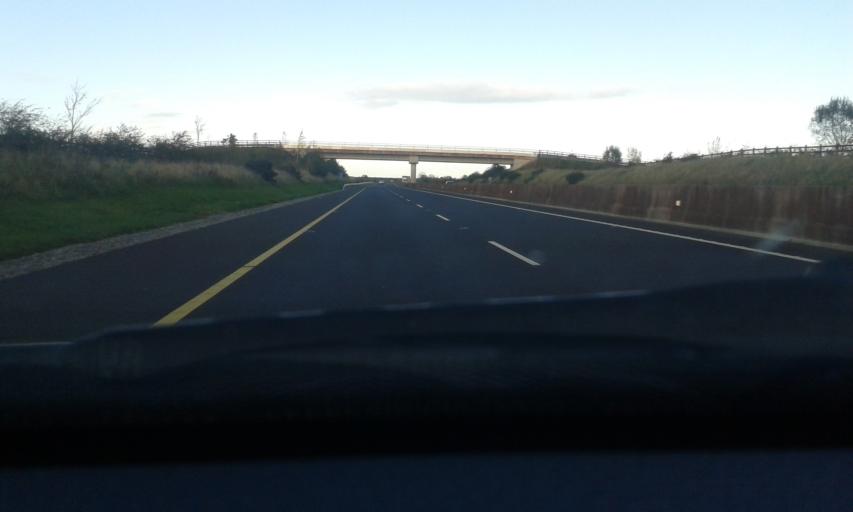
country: IE
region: Munster
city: Thurles
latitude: 52.6363
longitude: -7.7611
